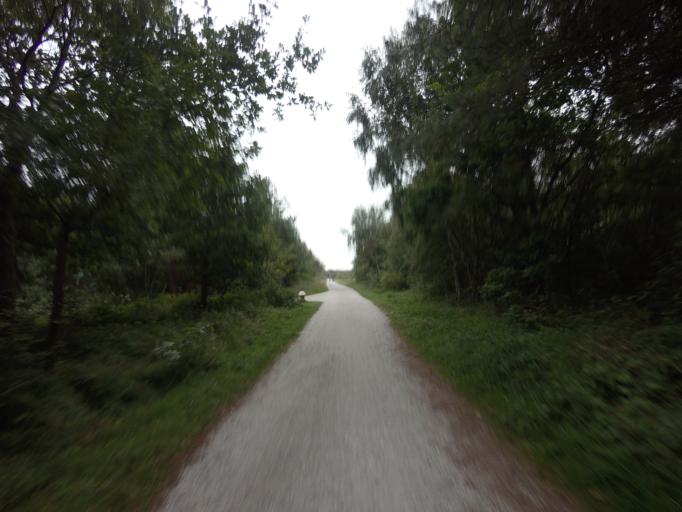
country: NL
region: Friesland
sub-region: Gemeente Schiermonnikoog
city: Schiermonnikoog
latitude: 53.4908
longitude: 6.1638
